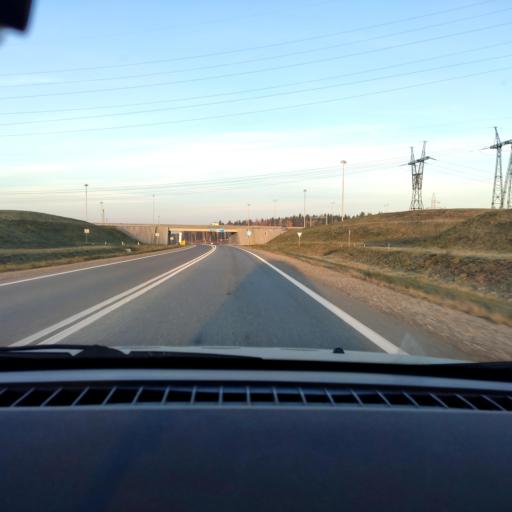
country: RU
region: Perm
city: Novyye Lyady
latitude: 58.0446
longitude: 56.4345
